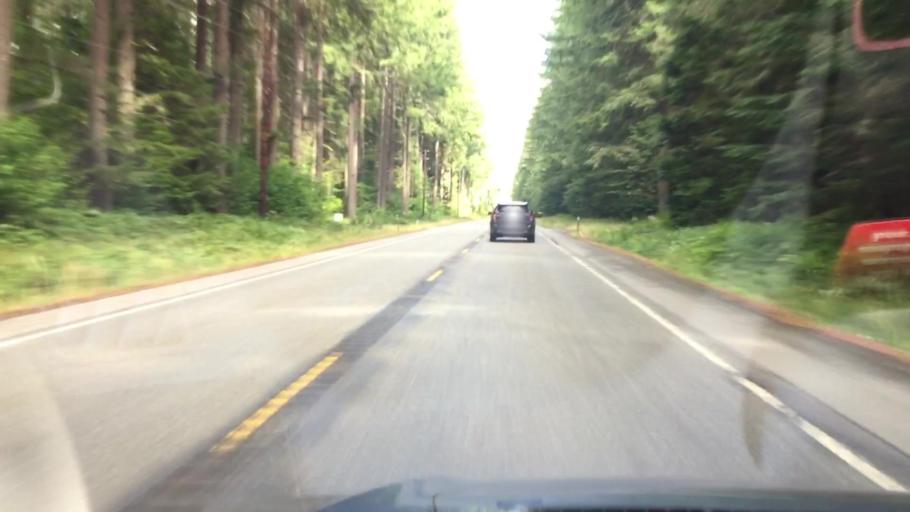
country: US
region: Washington
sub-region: Pierce County
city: Eatonville
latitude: 46.7561
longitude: -122.0859
